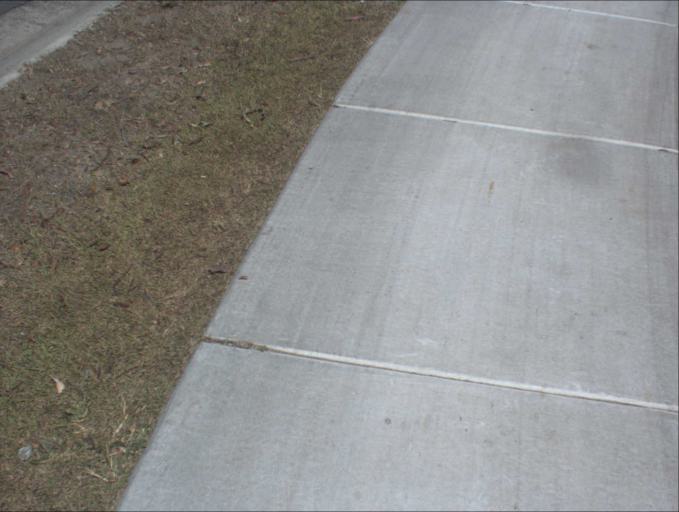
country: AU
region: Queensland
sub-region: Logan
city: Windaroo
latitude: -27.7427
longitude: 153.1970
